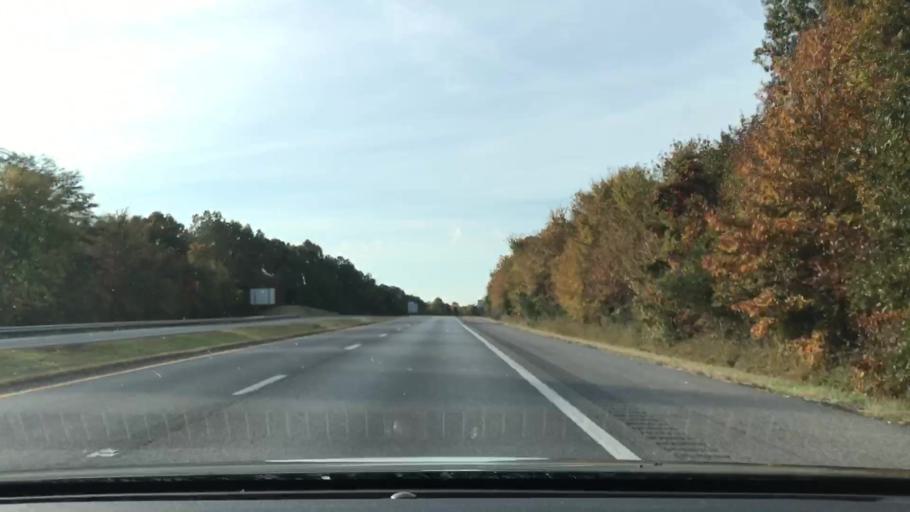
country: US
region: Kentucky
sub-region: Marshall County
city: Benton
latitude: 36.8607
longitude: -88.3673
